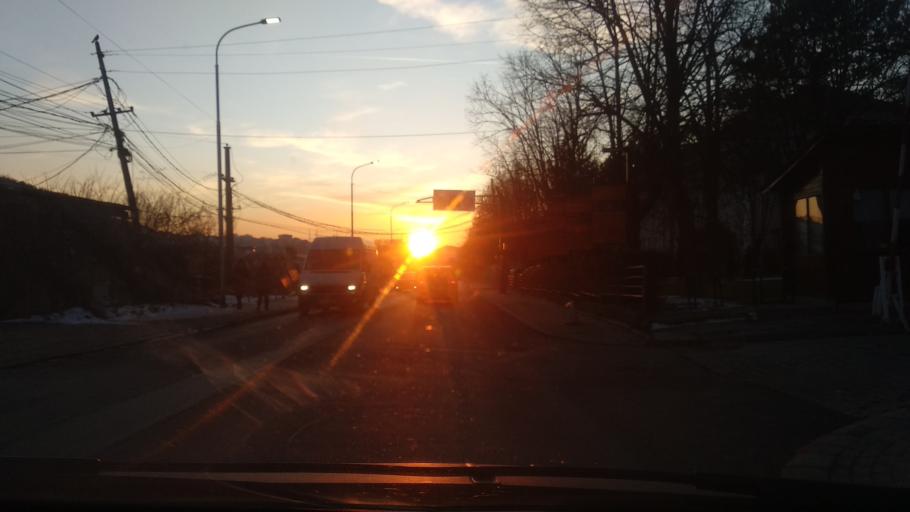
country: XK
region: Pristina
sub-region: Komuna e Prishtines
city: Pristina
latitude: 42.6698
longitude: 21.1921
